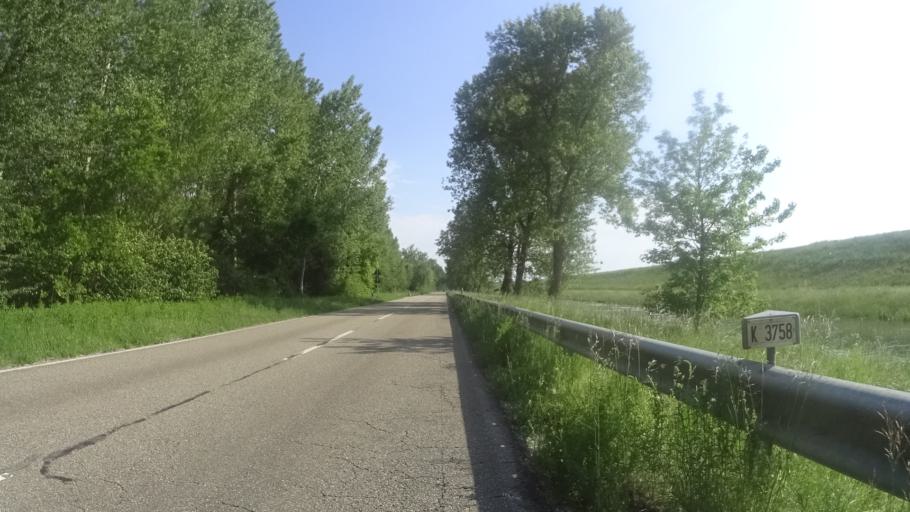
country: DE
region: Baden-Wuerttemberg
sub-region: Karlsruhe Region
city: Rheinmuenster
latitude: 48.7780
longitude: 8.0278
